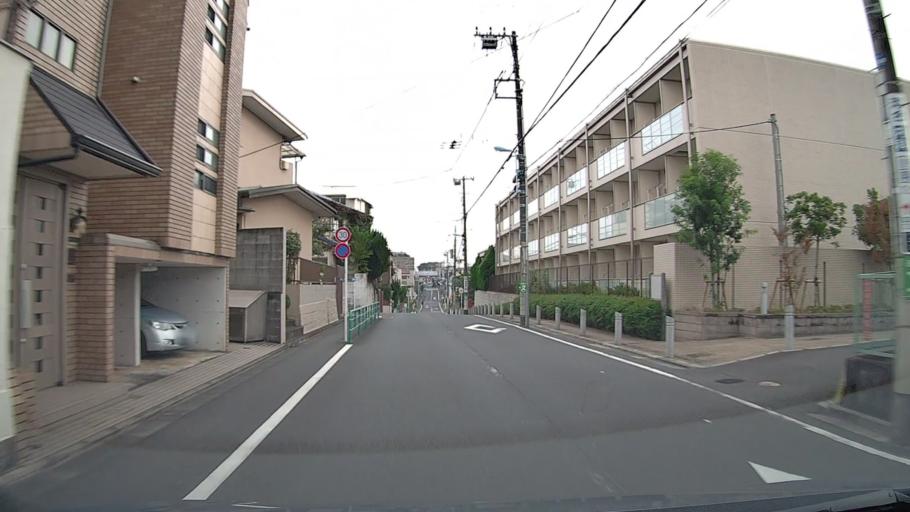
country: JP
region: Tokyo
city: Musashino
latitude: 35.7070
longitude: 139.6105
